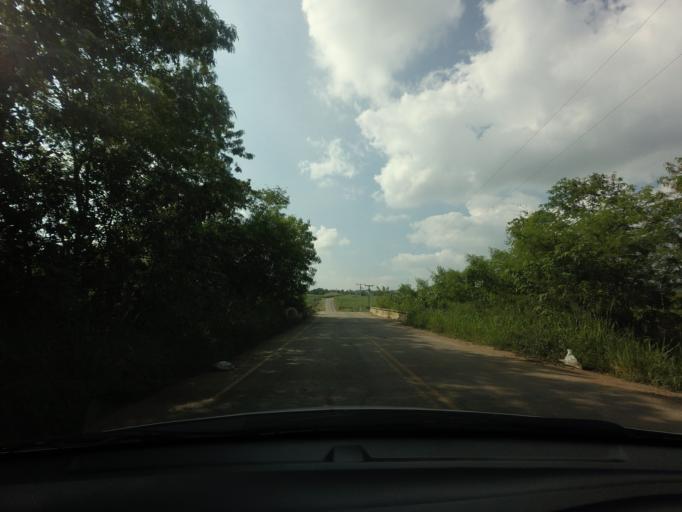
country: TH
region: Nakhon Ratchasima
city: Wang Nam Khiao
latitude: 14.5409
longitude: 101.6295
